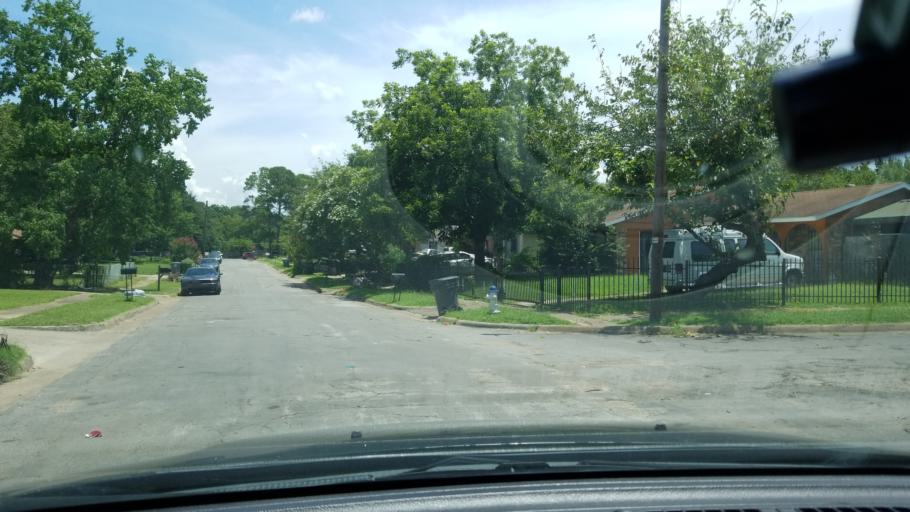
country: US
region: Texas
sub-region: Dallas County
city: Balch Springs
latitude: 32.7520
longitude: -96.6515
